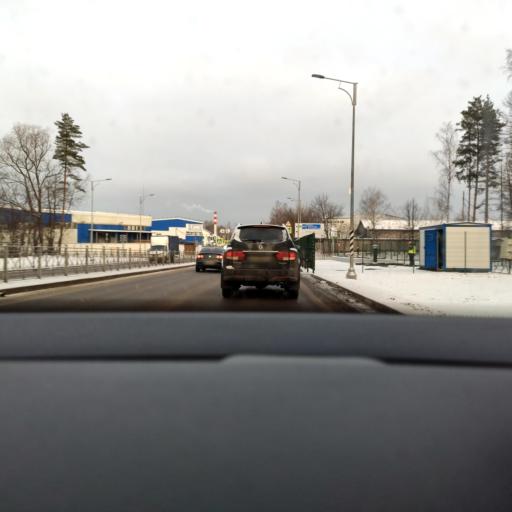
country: RU
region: Moskovskaya
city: Reutov
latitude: 55.7640
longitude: 37.8831
